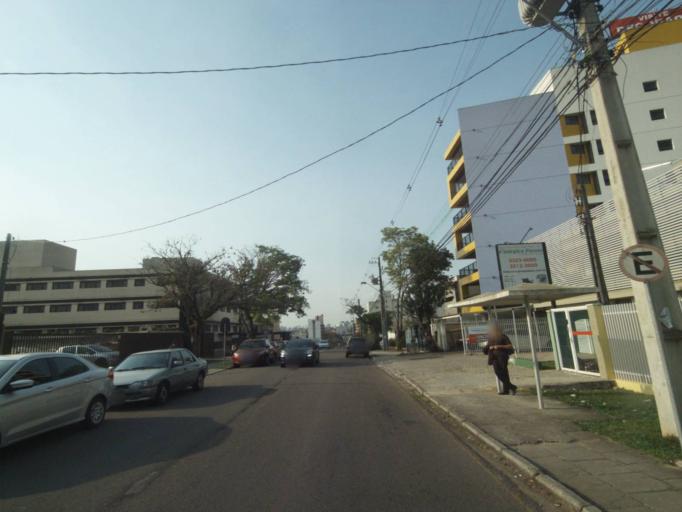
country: BR
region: Parana
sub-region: Curitiba
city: Curitiba
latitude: -25.4640
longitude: -49.2995
